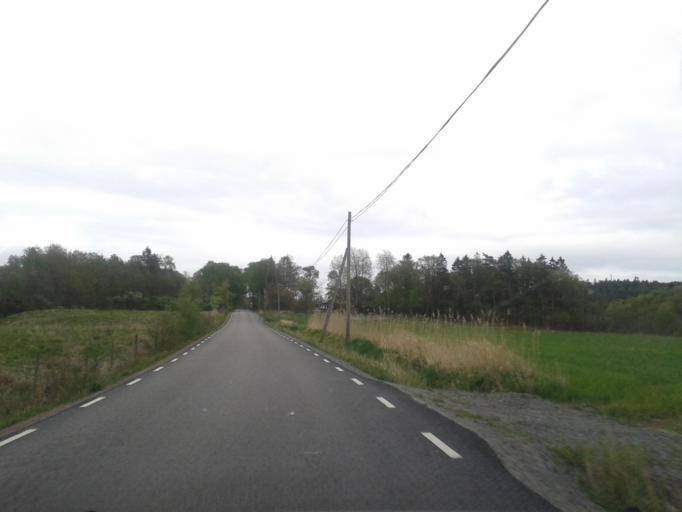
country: SE
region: Vaestra Goetaland
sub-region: Kungalvs Kommun
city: Kode
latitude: 57.9106
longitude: 11.8762
